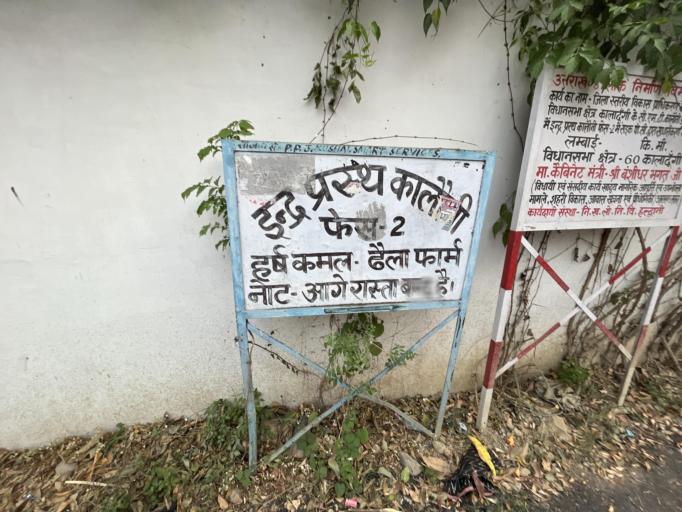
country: IN
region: Uttarakhand
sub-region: Naini Tal
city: Haldwani
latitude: 29.2033
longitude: 79.5108
